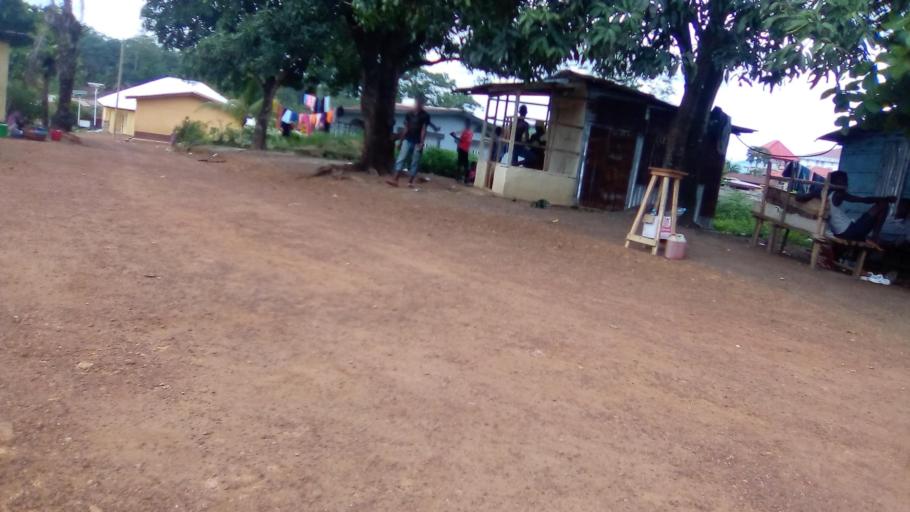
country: SL
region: Southern Province
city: Bo
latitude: 7.9575
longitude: -11.7455
